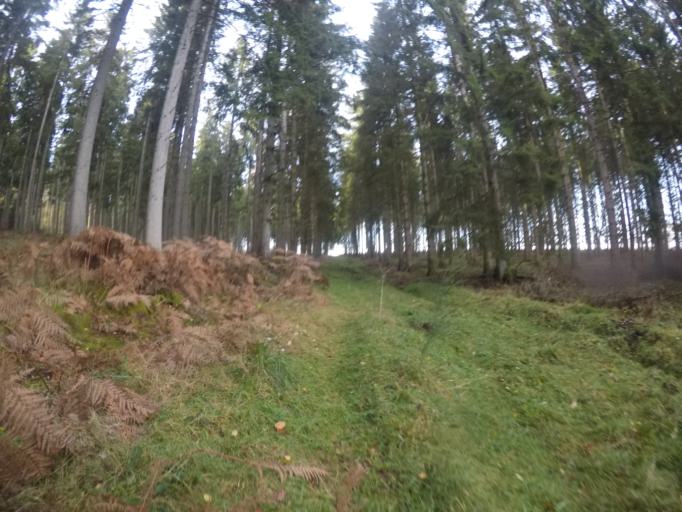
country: BE
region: Wallonia
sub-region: Province du Luxembourg
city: Habay-la-Vieille
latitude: 49.7644
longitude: 5.6047
